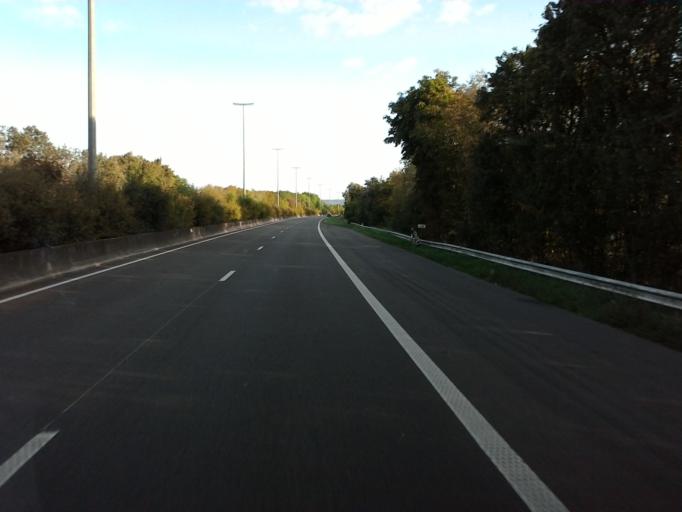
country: BE
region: Wallonia
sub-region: Province de Namur
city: Somme-Leuze
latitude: 50.3049
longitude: 5.3462
